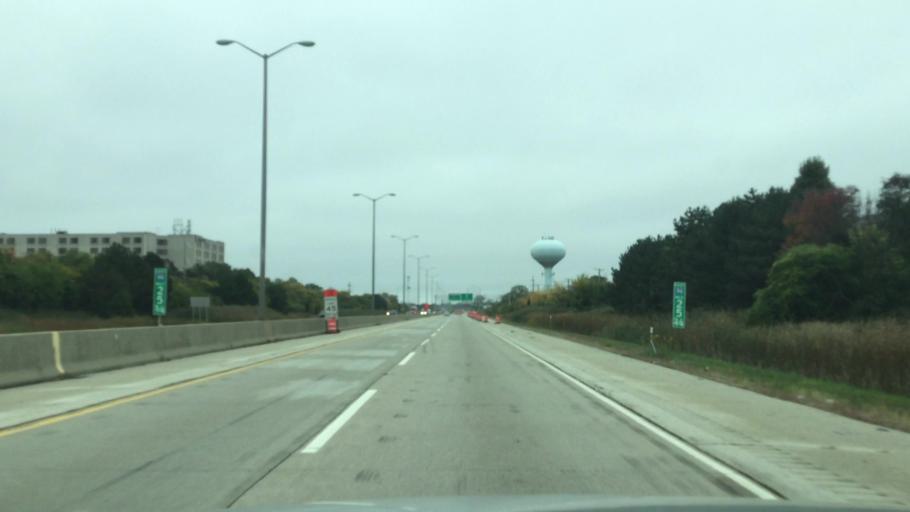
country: US
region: Illinois
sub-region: Lake County
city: Deerfield
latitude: 42.1495
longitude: -87.8681
